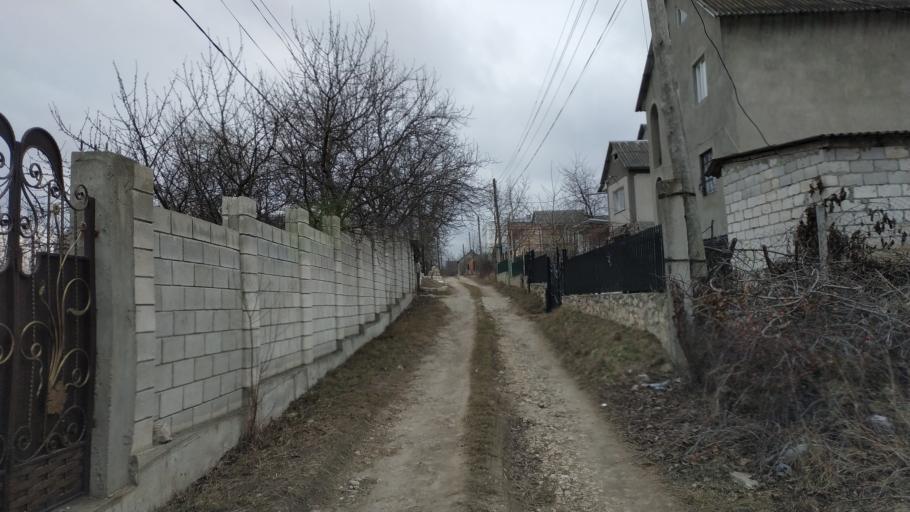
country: MD
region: Laloveni
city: Ialoveni
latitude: 46.9312
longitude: 28.7951
